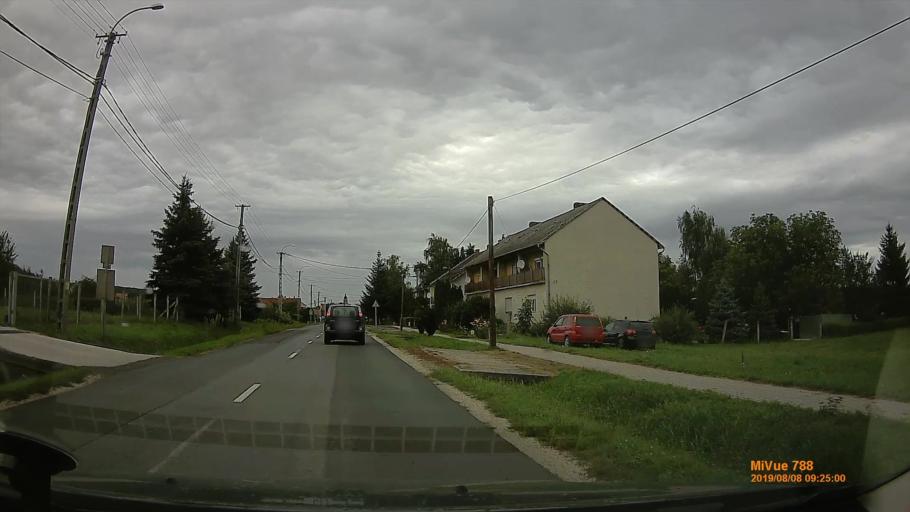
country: HU
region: Zala
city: Zalaegerszeg
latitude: 46.9290
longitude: 16.8569
